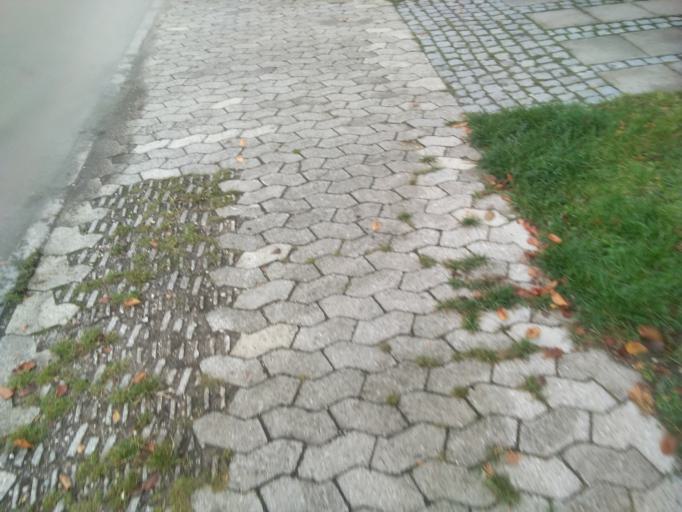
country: DK
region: Capital Region
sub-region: Gladsaxe Municipality
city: Buddinge
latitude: 55.7271
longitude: 12.5049
